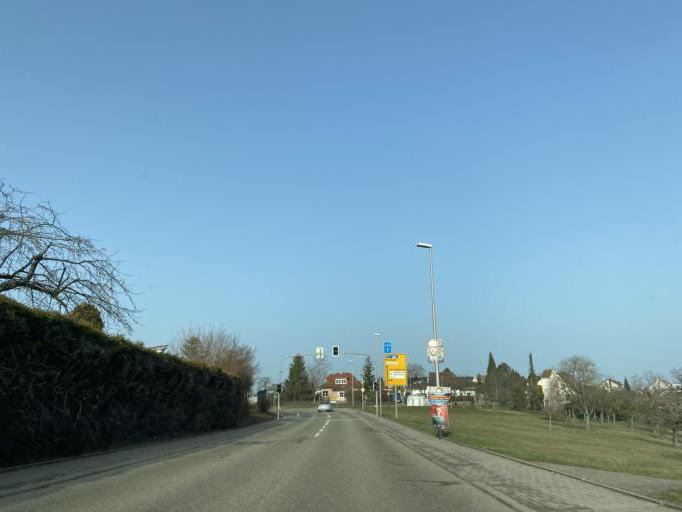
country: DE
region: Baden-Wuerttemberg
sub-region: Karlsruhe Region
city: Wurmberg
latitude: 48.8718
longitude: 8.8111
